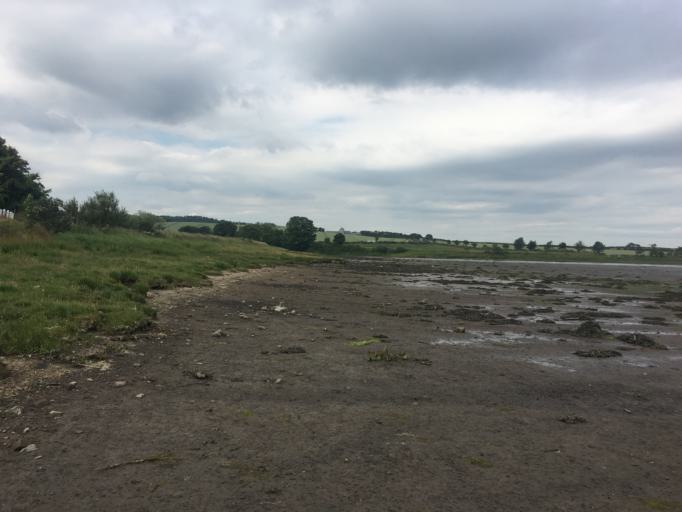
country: GB
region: England
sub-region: Northumberland
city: Bamburgh
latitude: 55.6043
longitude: -1.7654
